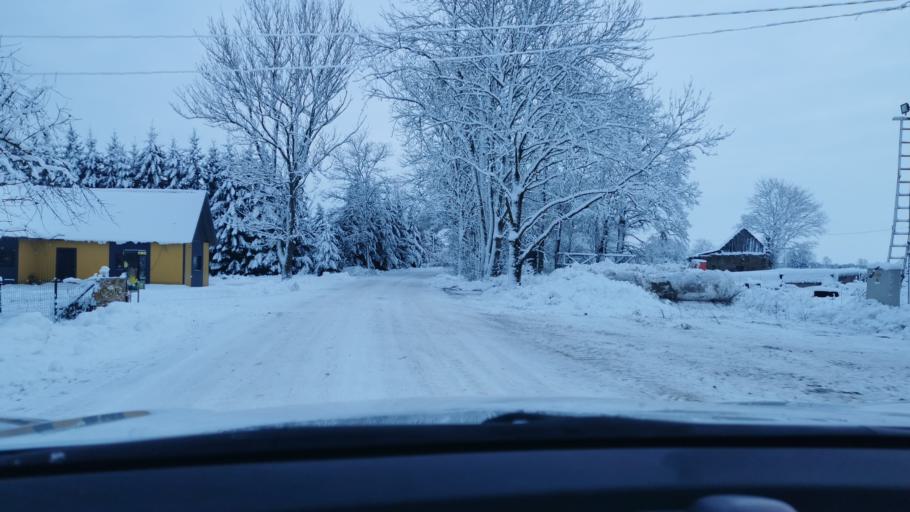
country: EE
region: Laeaene-Virumaa
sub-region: Haljala vald
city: Haljala
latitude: 59.4841
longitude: 26.3308
